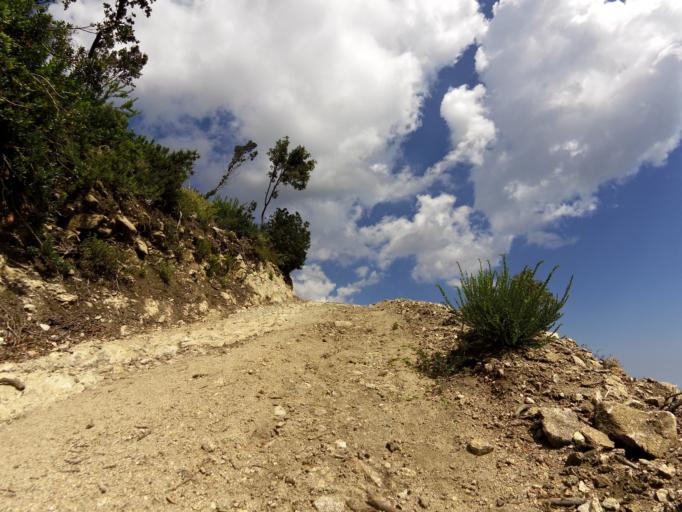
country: IT
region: Calabria
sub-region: Provincia di Vibo-Valentia
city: Nardodipace
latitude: 38.5038
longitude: 16.3938
